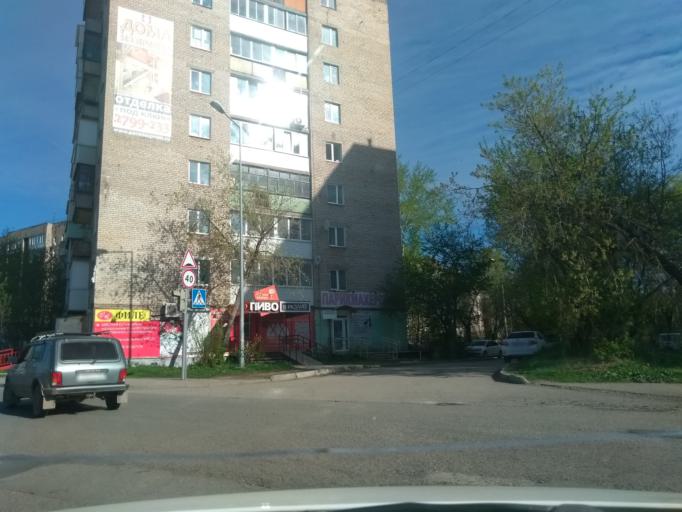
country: RU
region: Perm
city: Perm
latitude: 57.9865
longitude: 56.2681
